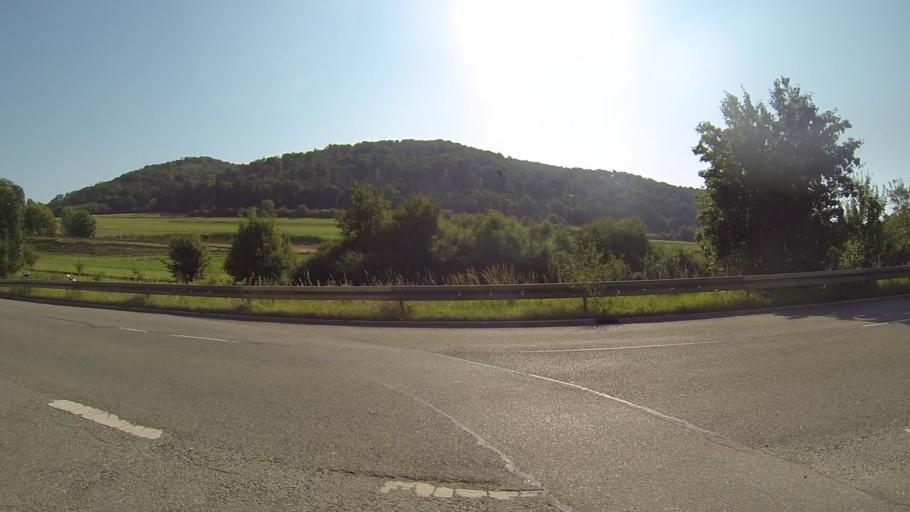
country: DE
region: Baden-Wuerttemberg
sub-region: Regierungsbezirk Stuttgart
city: Oberkochen
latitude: 48.7731
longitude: 10.0995
